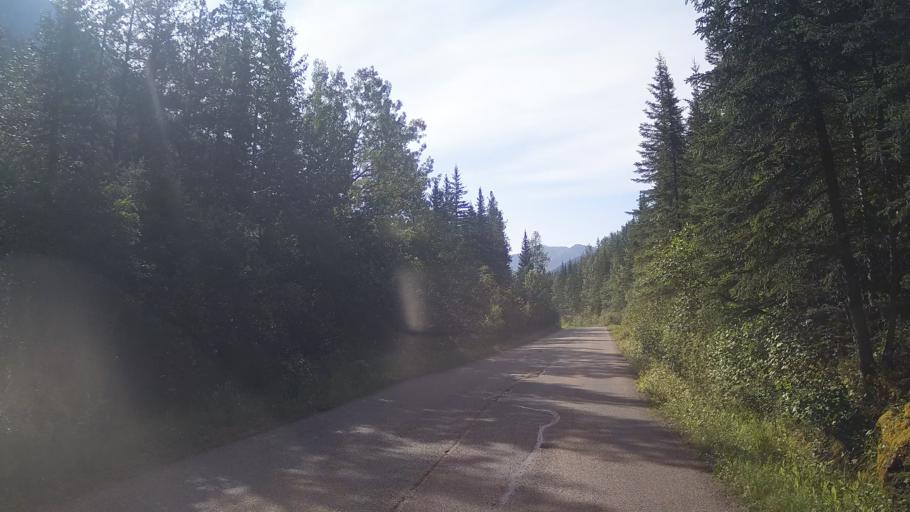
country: CA
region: Alberta
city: Hinton
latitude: 53.1774
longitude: -117.8331
